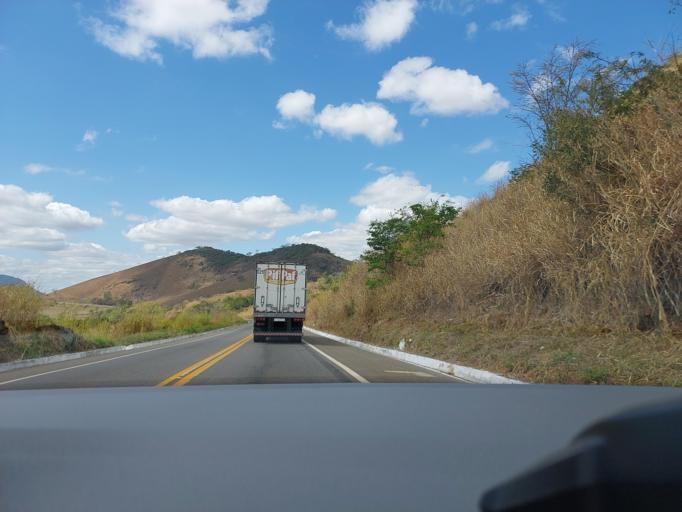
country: BR
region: Minas Gerais
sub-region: Muriae
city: Muriae
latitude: -21.1273
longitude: -42.2465
